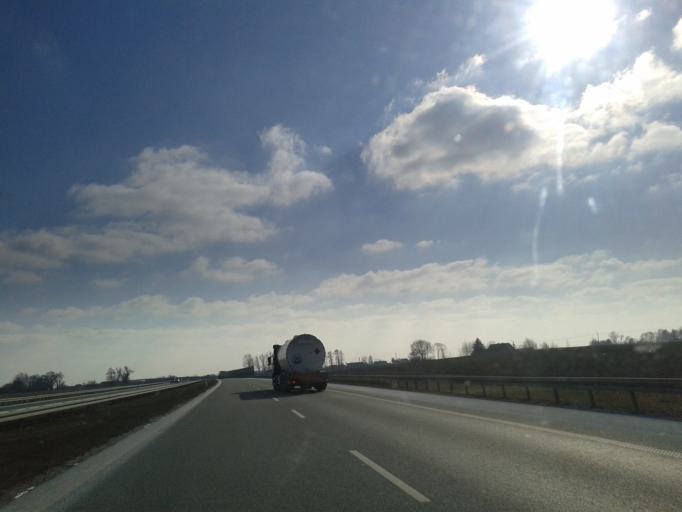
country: PL
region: Kujawsko-Pomorskie
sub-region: Powiat aleksandrowski
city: Waganiec
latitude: 52.7791
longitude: 18.8436
